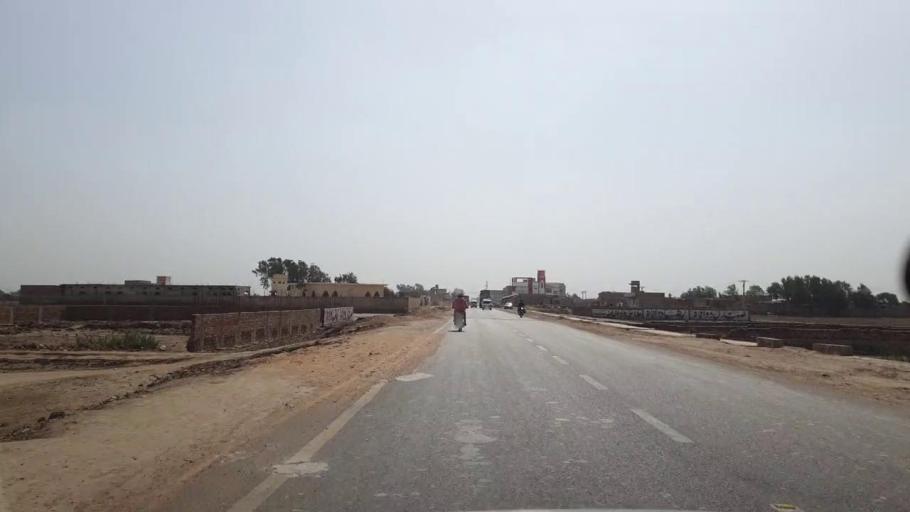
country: PK
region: Sindh
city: Matli
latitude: 25.0559
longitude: 68.6422
